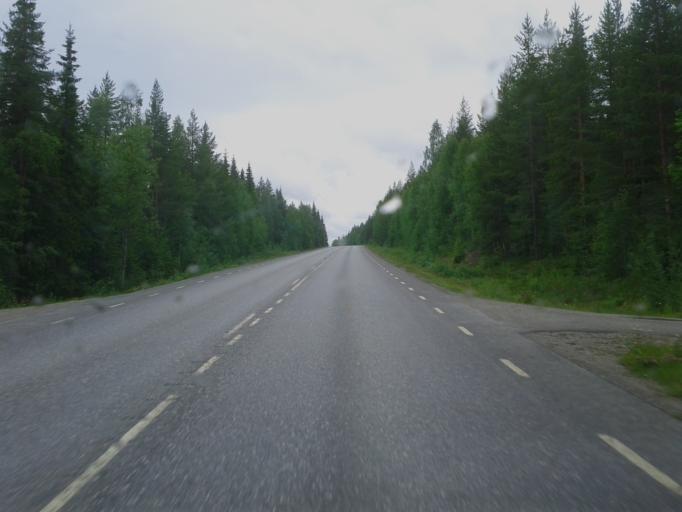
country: SE
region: Vaesterbotten
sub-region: Skelleftea Kommun
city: Langsele
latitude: 64.8983
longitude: 20.1482
